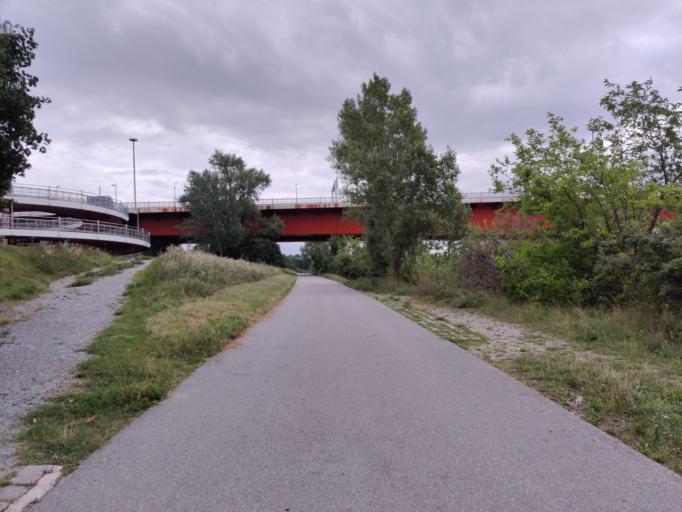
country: AT
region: Vienna
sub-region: Wien Stadt
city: Vienna
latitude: 48.2394
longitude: 16.3950
